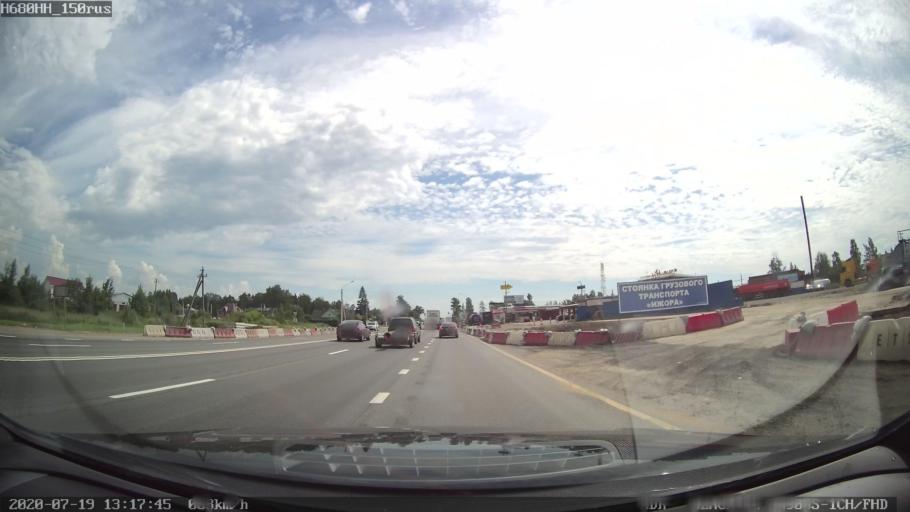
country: RU
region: St.-Petersburg
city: Kolpino
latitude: 59.7062
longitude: 30.5748
